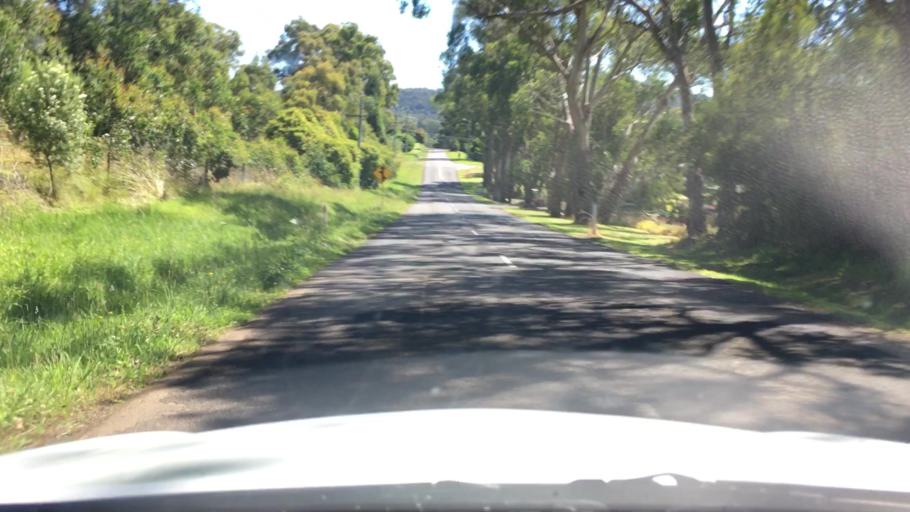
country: AU
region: Victoria
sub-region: Yarra Ranges
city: Mount Evelyn
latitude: -37.7995
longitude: 145.4201
